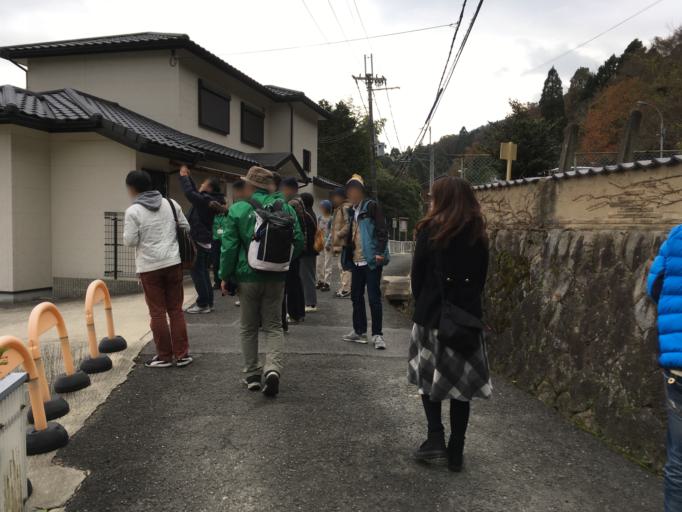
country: JP
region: Nara
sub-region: Ikoma-shi
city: Ikoma
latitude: 34.6879
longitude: 135.6878
